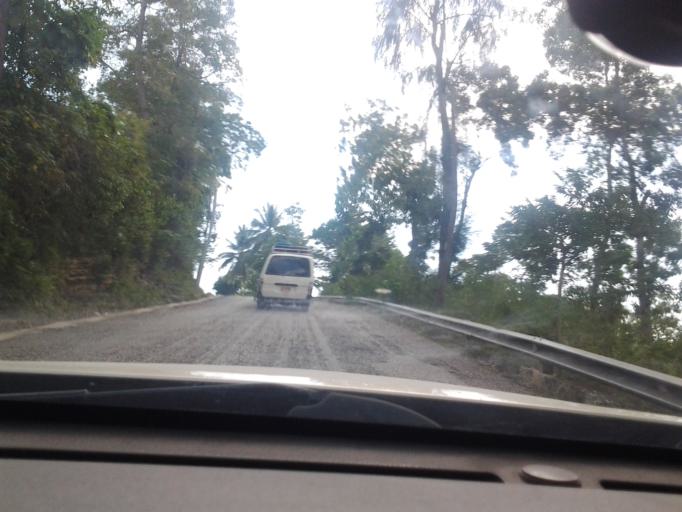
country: HT
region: Sud-Est
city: Jacmel
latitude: 18.3144
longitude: -72.5811
